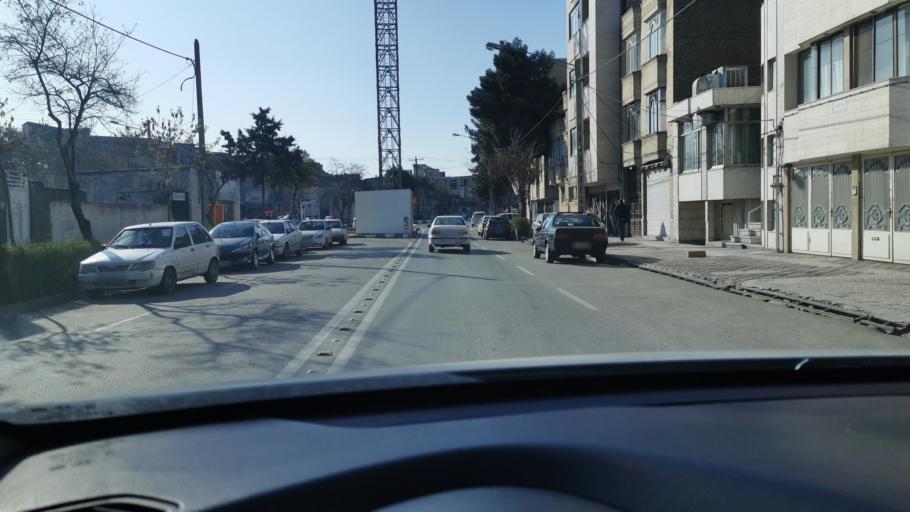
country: IR
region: Razavi Khorasan
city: Mashhad
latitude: 36.2762
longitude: 59.5759
